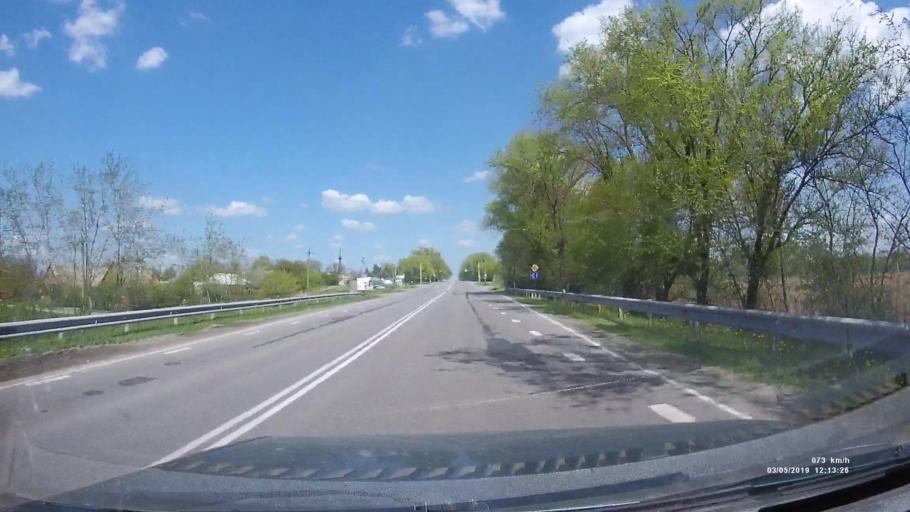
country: RU
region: Rostov
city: Melikhovskaya
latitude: 47.3326
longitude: 40.5549
